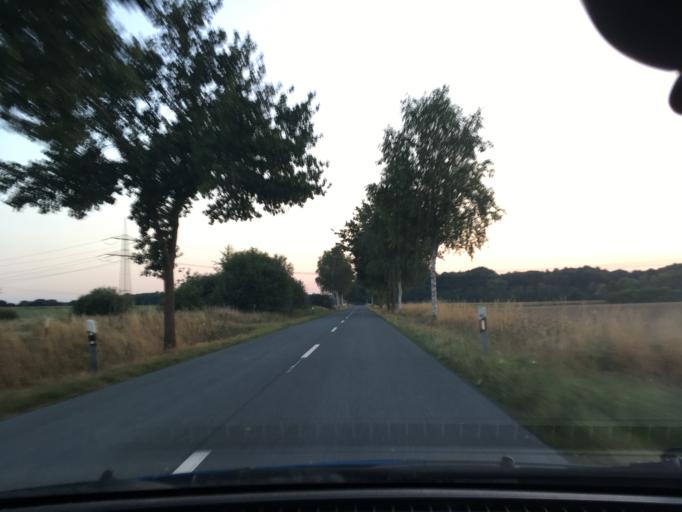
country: DE
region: Lower Saxony
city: Barnstedt
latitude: 53.1367
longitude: 10.3895
